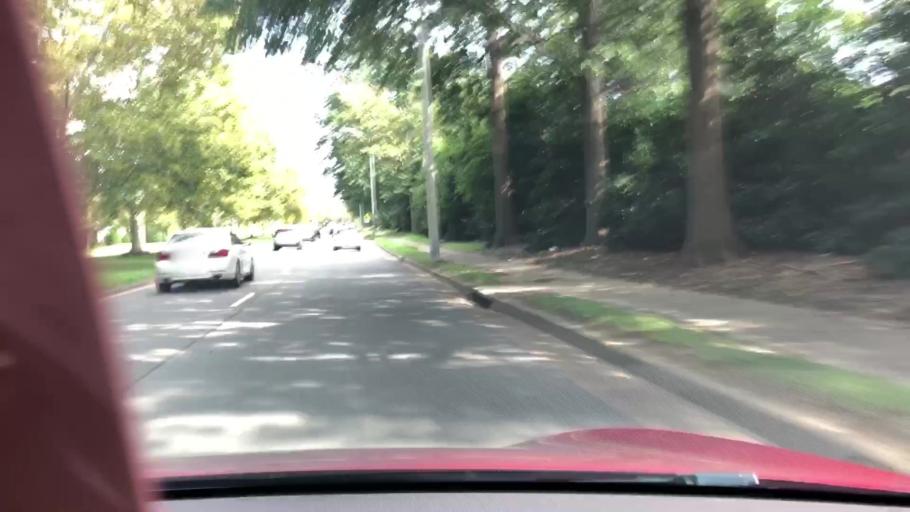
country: US
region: Virginia
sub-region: City of Virginia Beach
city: Virginia Beach
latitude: 36.8910
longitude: -76.0541
